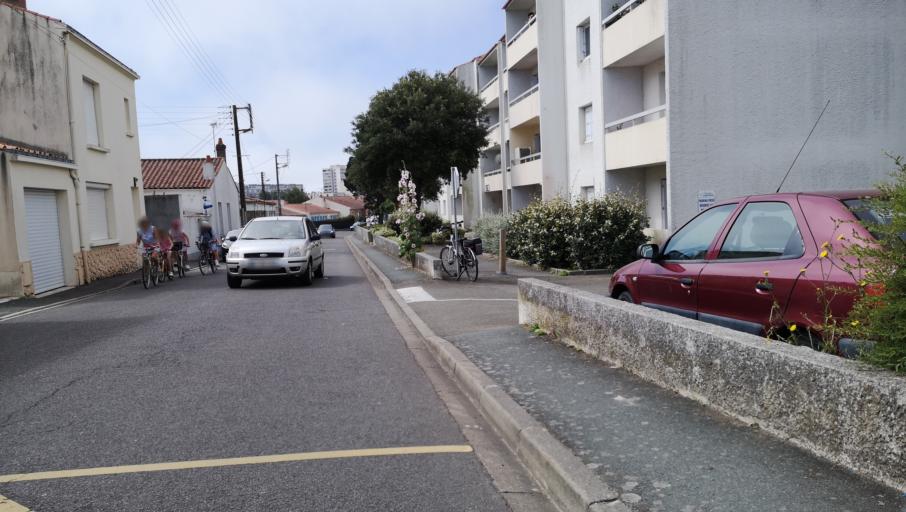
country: FR
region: Pays de la Loire
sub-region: Departement de la Vendee
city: Les Sables-d'Olonne
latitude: 46.5039
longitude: -1.7830
